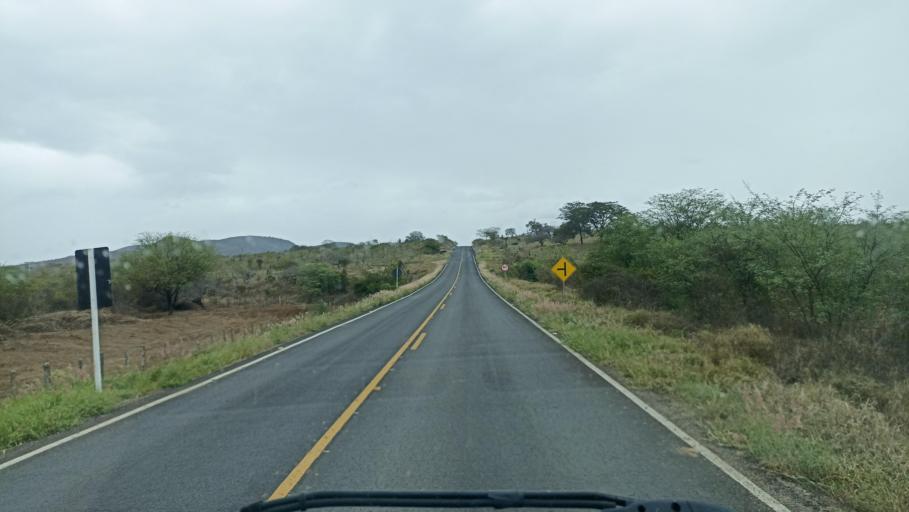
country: BR
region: Bahia
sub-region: Andarai
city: Vera Cruz
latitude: -13.0489
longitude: -40.7492
